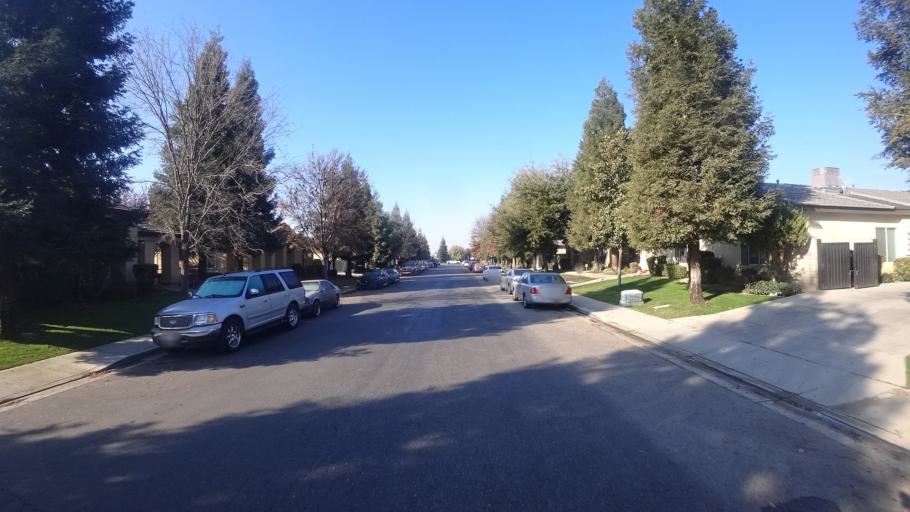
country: US
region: California
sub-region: Kern County
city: Greenacres
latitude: 35.3100
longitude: -119.1121
